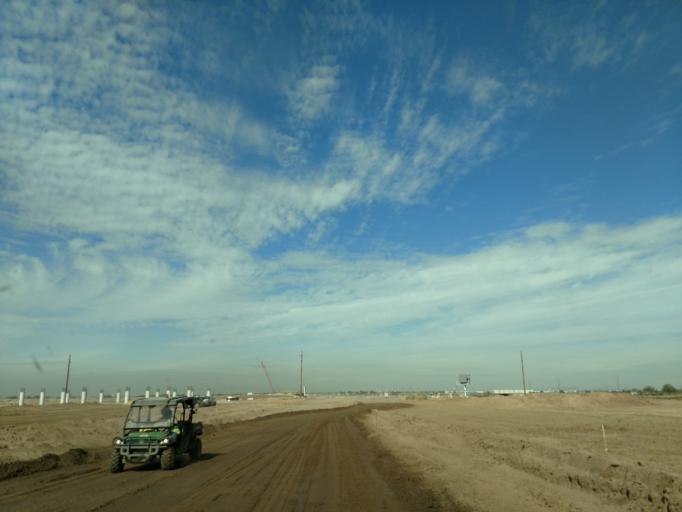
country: US
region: Arizona
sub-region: Maricopa County
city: Laveen
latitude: 33.3903
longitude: -112.1913
